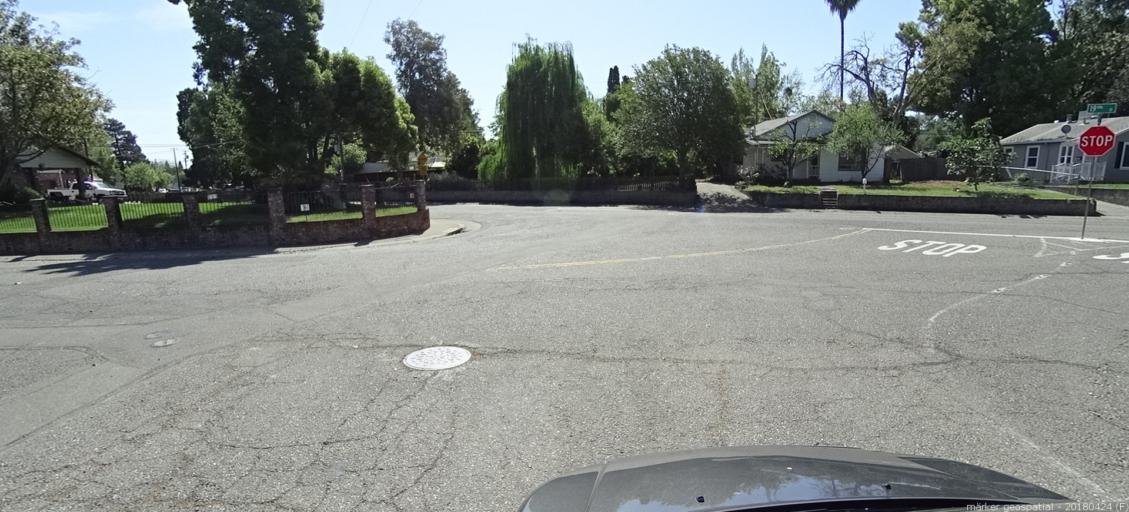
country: US
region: California
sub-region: Yolo County
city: West Sacramento
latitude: 38.5647
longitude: -121.5300
